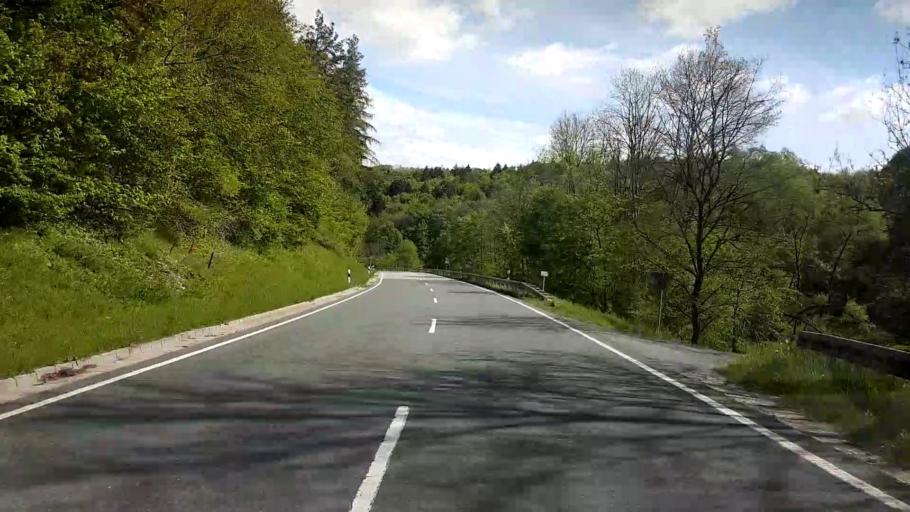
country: DE
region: Bavaria
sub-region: Upper Franconia
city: Ebermannstadt
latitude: 49.8071
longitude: 11.1468
